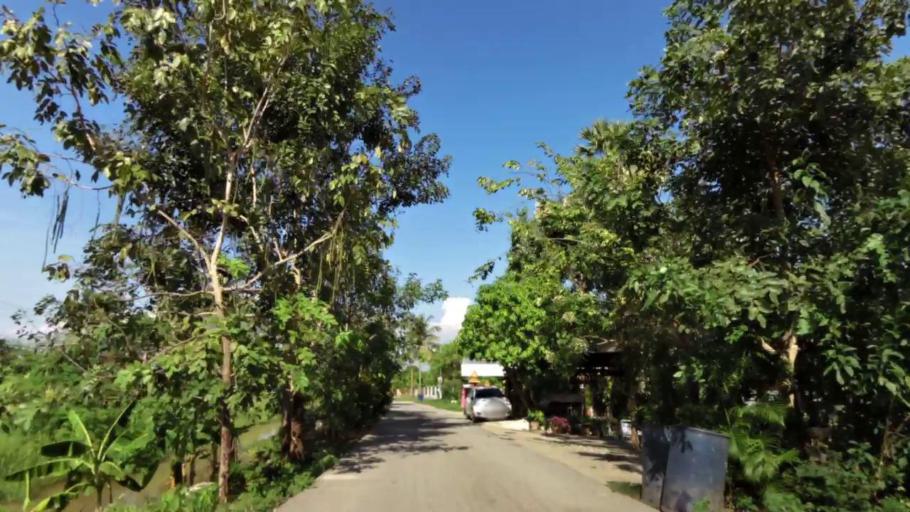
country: TH
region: Ang Thong
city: Ang Thong
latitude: 14.5884
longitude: 100.4688
